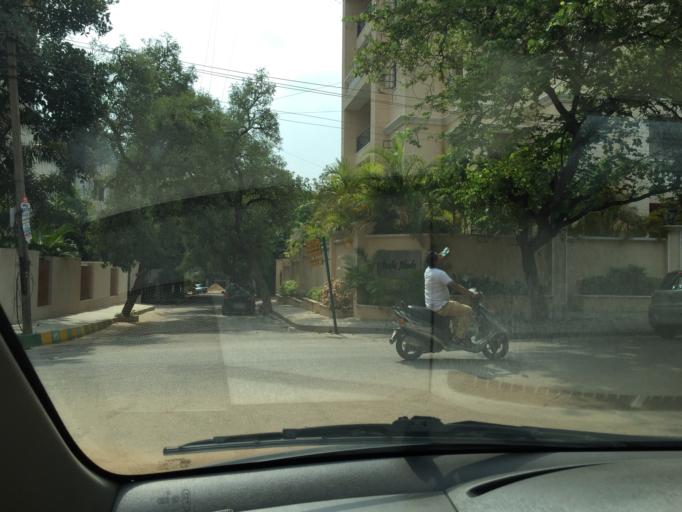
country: IN
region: Karnataka
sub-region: Bangalore Urban
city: Bangalore
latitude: 12.9997
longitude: 77.6231
